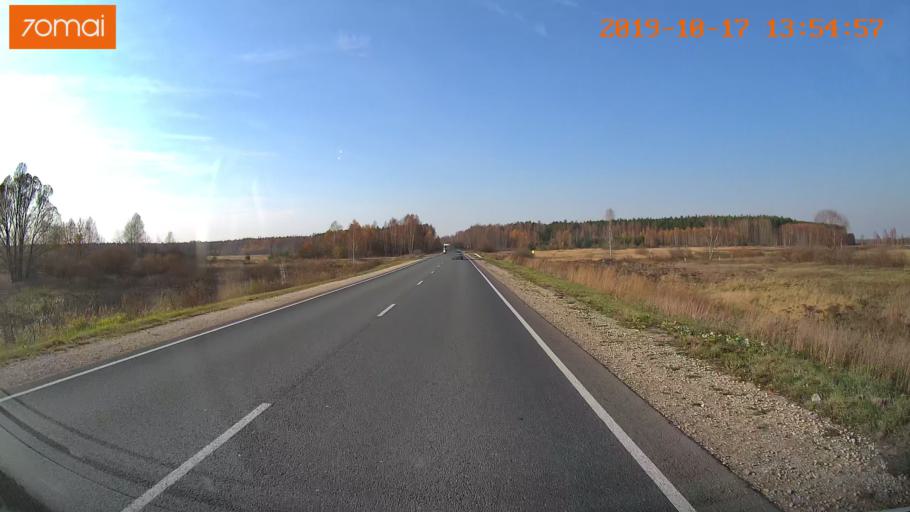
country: RU
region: Rjazan
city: Spas-Klepiki
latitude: 55.1492
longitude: 40.3010
